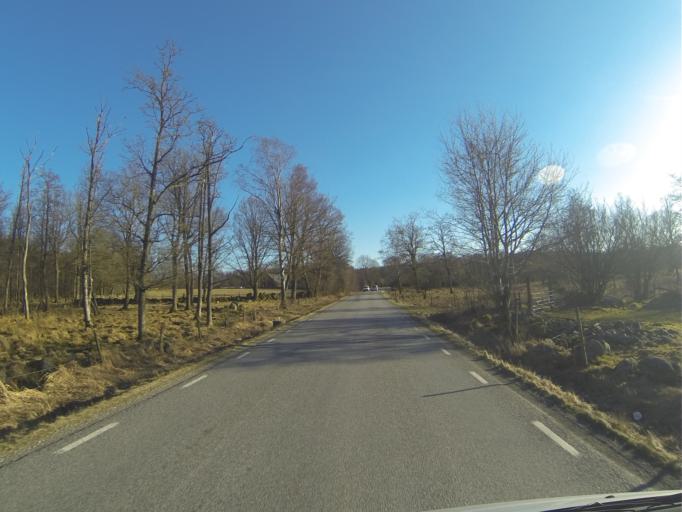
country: SE
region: Skane
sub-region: Horby Kommun
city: Hoerby
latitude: 55.8921
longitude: 13.6667
